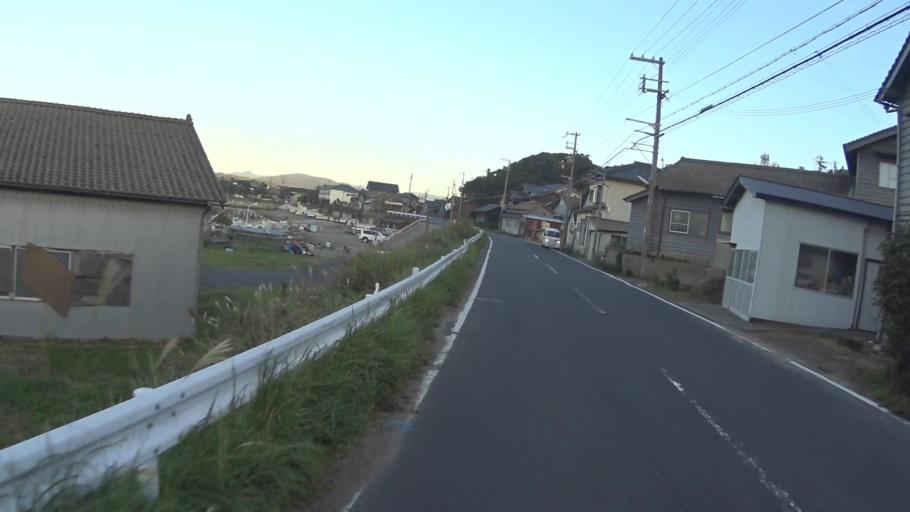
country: JP
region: Kyoto
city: Miyazu
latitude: 35.6904
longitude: 135.0143
